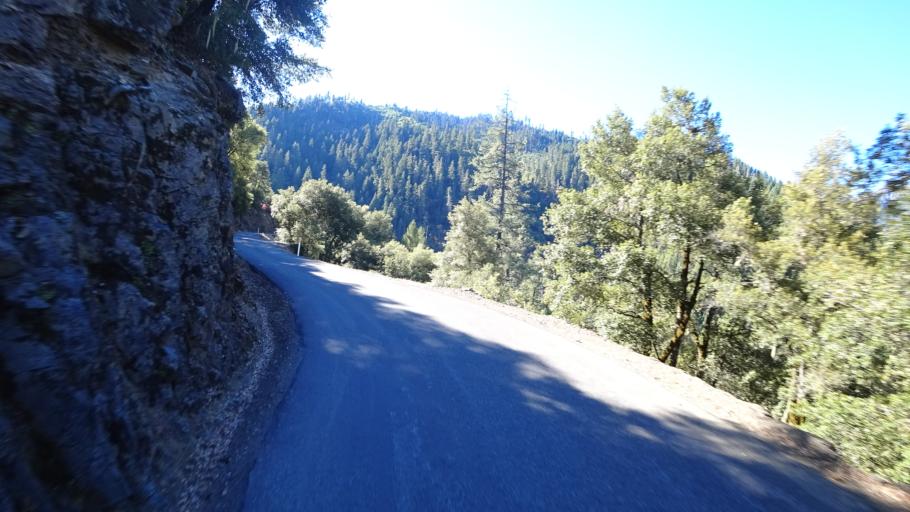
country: US
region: California
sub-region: Humboldt County
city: Willow Creek
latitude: 41.1497
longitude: -123.2097
